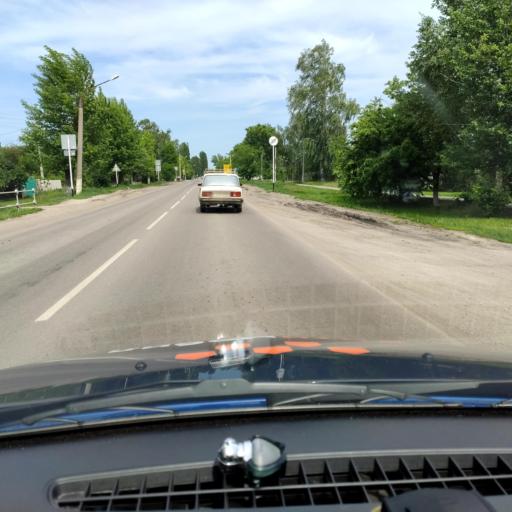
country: RU
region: Voronezj
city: Maslovka
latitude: 51.5387
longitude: 39.3381
